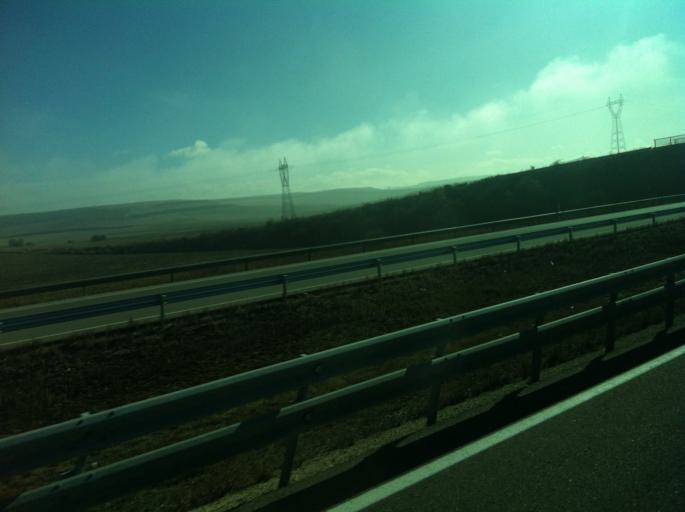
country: ES
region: Castille and Leon
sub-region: Provincia de Burgos
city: Rubena
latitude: 42.3699
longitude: -3.5892
